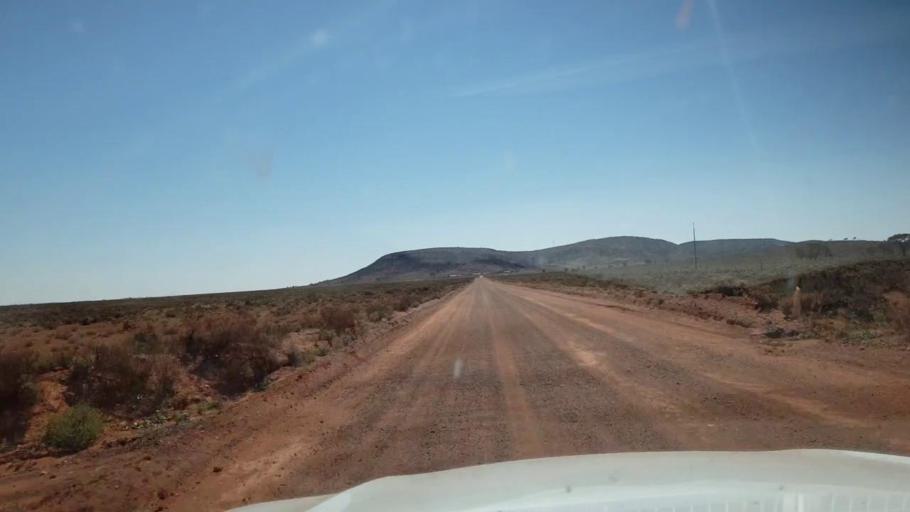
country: AU
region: South Australia
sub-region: Whyalla
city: Whyalla
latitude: -32.7047
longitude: 137.1367
